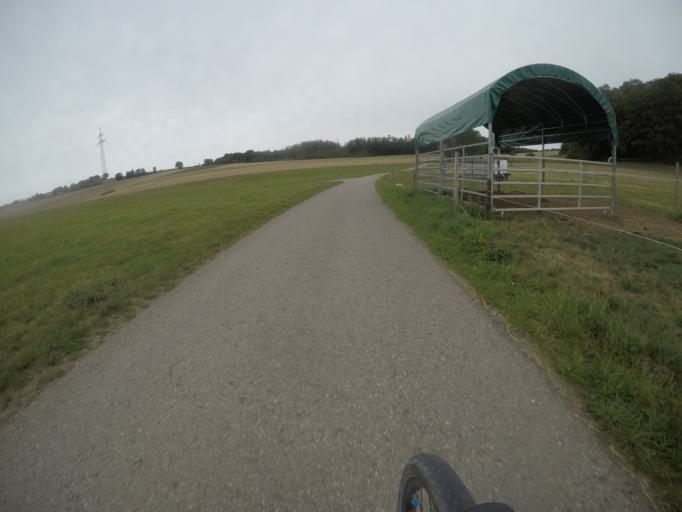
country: DE
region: Baden-Wuerttemberg
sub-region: Karlsruhe Region
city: Wurmberg
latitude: 48.8690
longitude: 8.8330
